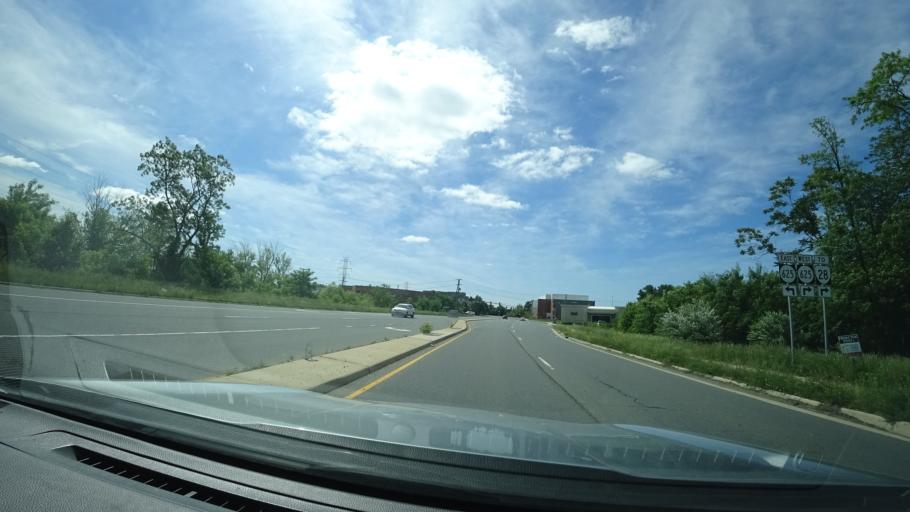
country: US
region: Virginia
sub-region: Loudoun County
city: Sterling
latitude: 39.0067
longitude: -77.4300
